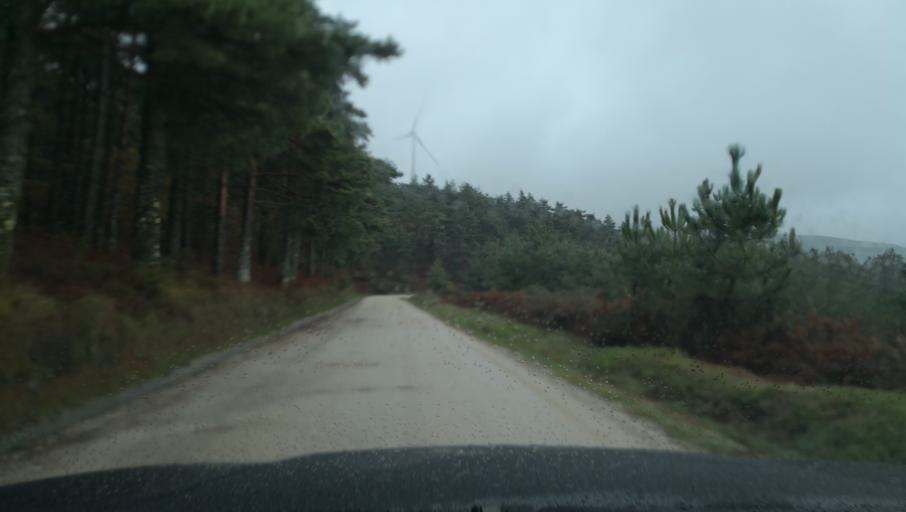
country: PT
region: Vila Real
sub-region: Mondim de Basto
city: Mondim de Basto
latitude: 41.3181
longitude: -7.8819
